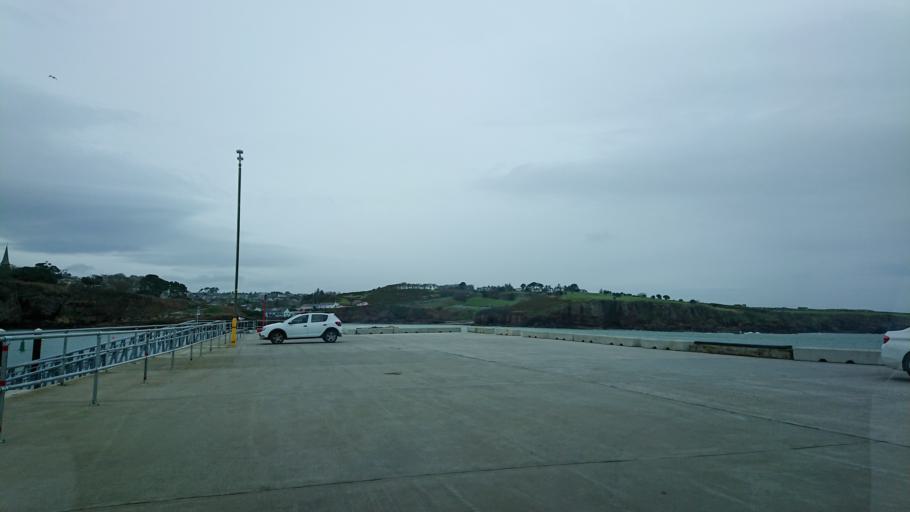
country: IE
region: Munster
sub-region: Waterford
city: Dunmore East
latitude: 52.1492
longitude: -6.9895
